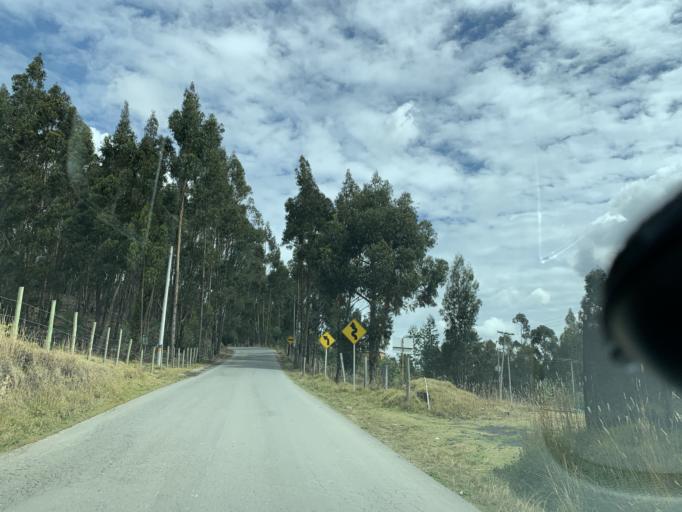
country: CO
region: Boyaca
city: Siachoque
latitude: 5.5689
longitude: -73.2666
